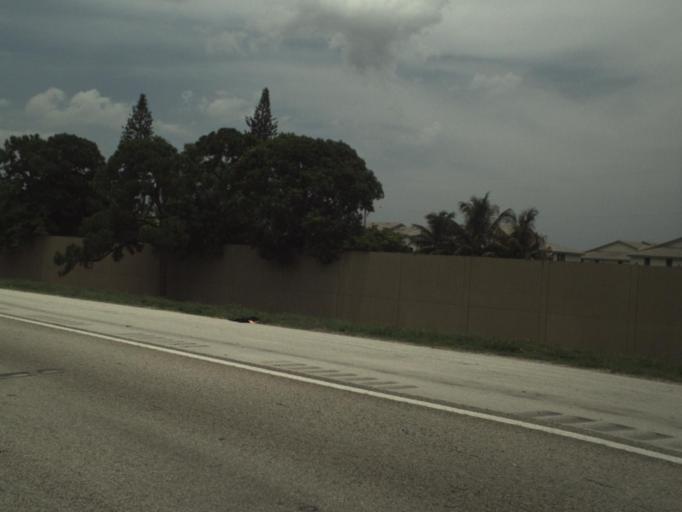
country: US
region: Florida
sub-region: Broward County
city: North Andrews Gardens
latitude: 26.2134
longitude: -80.1363
